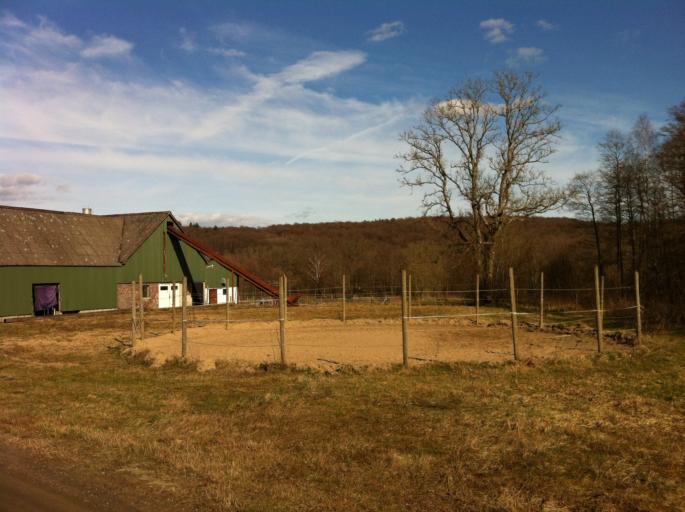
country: SE
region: Skane
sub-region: Hassleholms Kommun
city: Tormestorp
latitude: 56.0899
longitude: 13.7351
